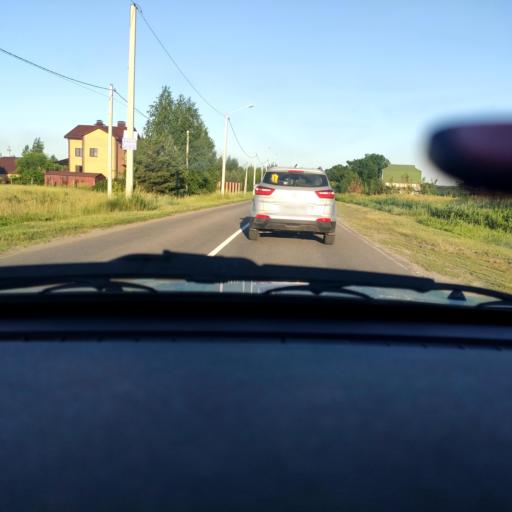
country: RU
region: Voronezj
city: Ramon'
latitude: 51.8927
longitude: 39.2560
